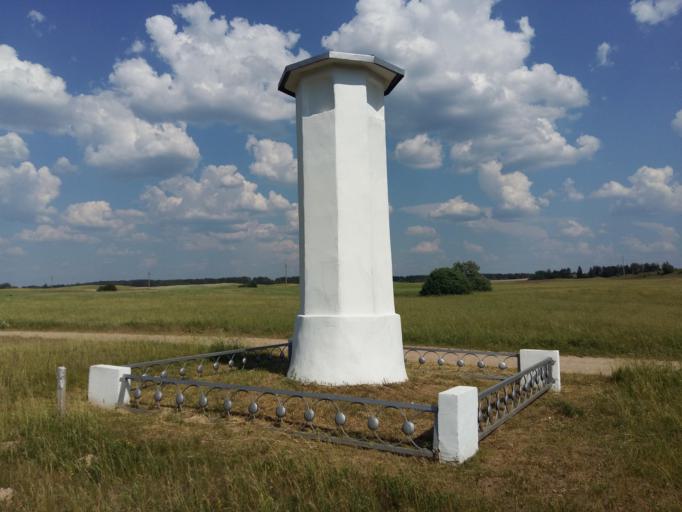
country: LT
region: Alytaus apskritis
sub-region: Alytaus rajonas
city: Daugai
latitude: 54.1775
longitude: 24.1913
